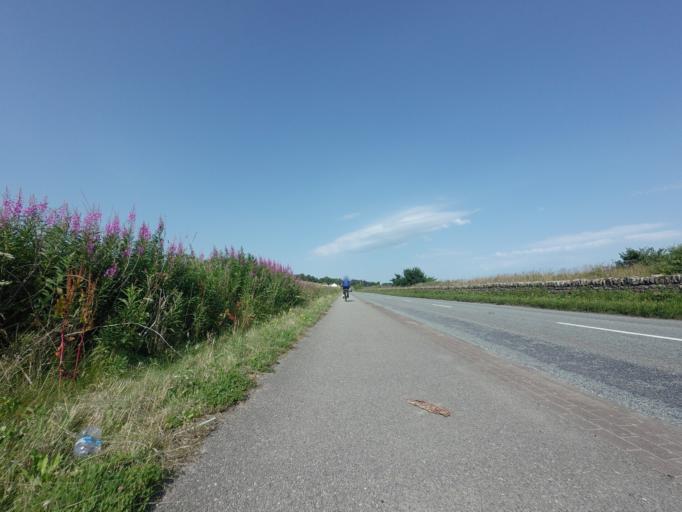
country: GB
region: Scotland
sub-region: Highland
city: Alness
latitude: 57.6862
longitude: -4.2853
